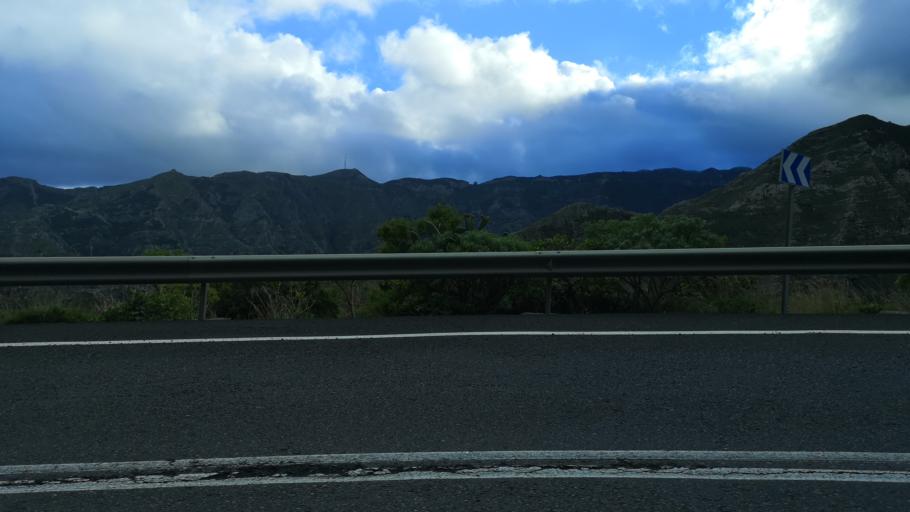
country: ES
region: Canary Islands
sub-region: Provincia de Santa Cruz de Tenerife
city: Hermigua
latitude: 28.1299
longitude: -17.1779
